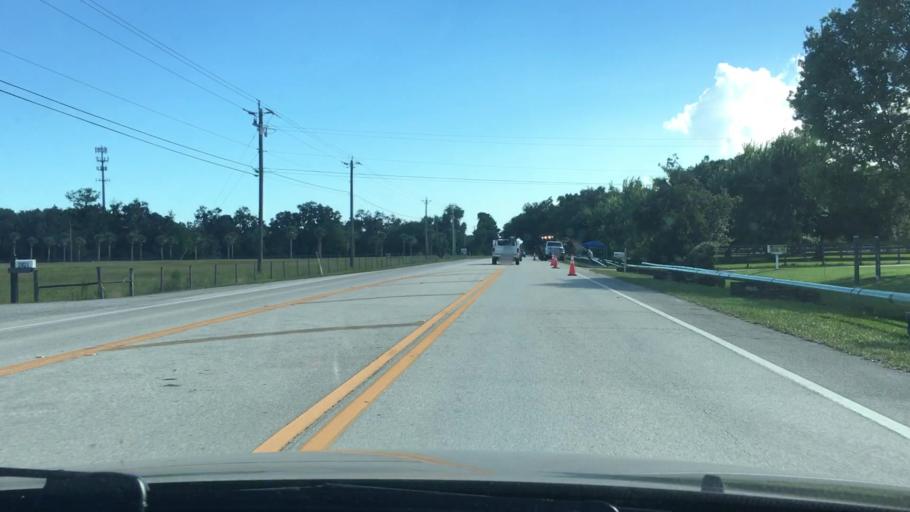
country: US
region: Florida
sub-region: Volusia County
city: Samsula-Spruce Creek
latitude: 29.0906
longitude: -81.0686
